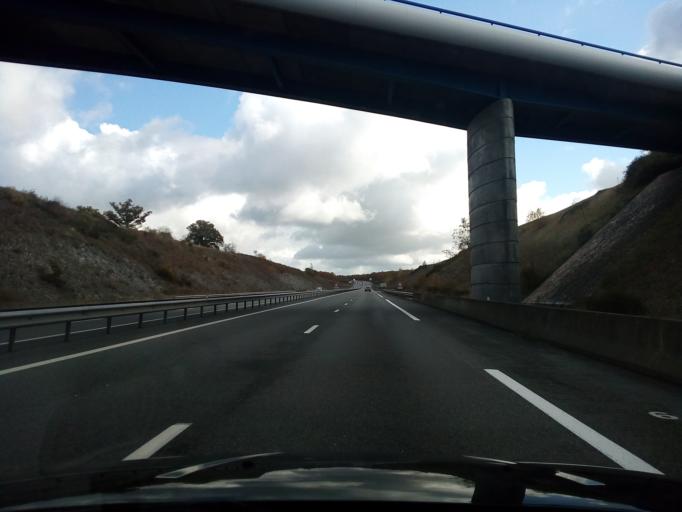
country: FR
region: Limousin
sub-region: Departement de la Creuse
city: Gouzon
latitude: 46.1953
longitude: 2.1596
